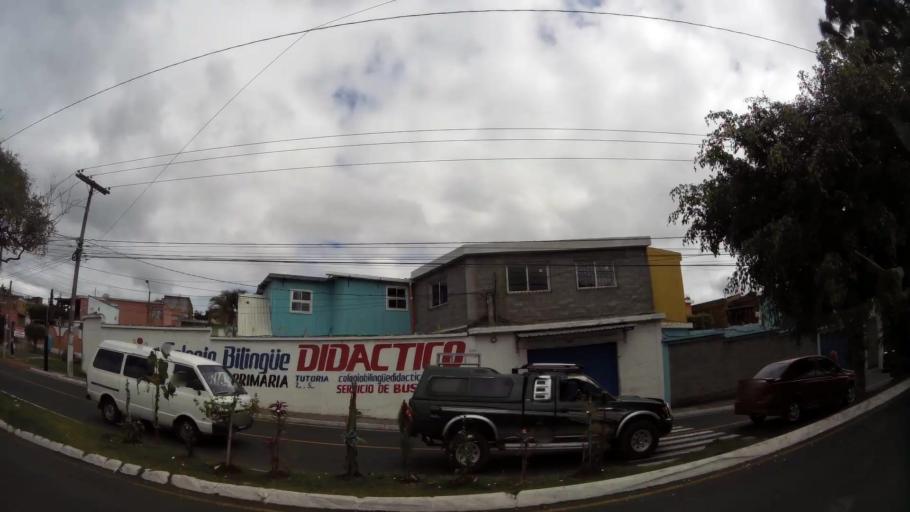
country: GT
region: Guatemala
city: Guatemala City
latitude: 14.6359
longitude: -90.5504
